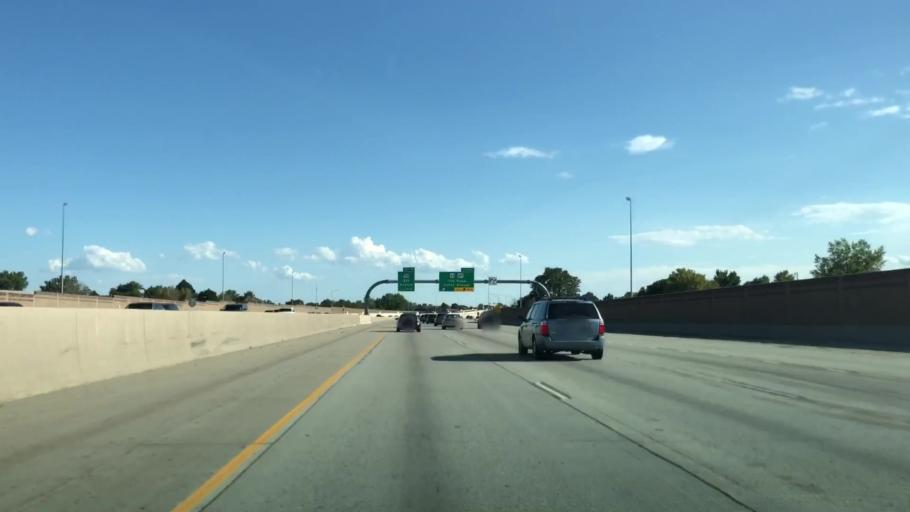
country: US
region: Colorado
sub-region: Adams County
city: Aurora
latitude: 39.7512
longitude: -104.8269
